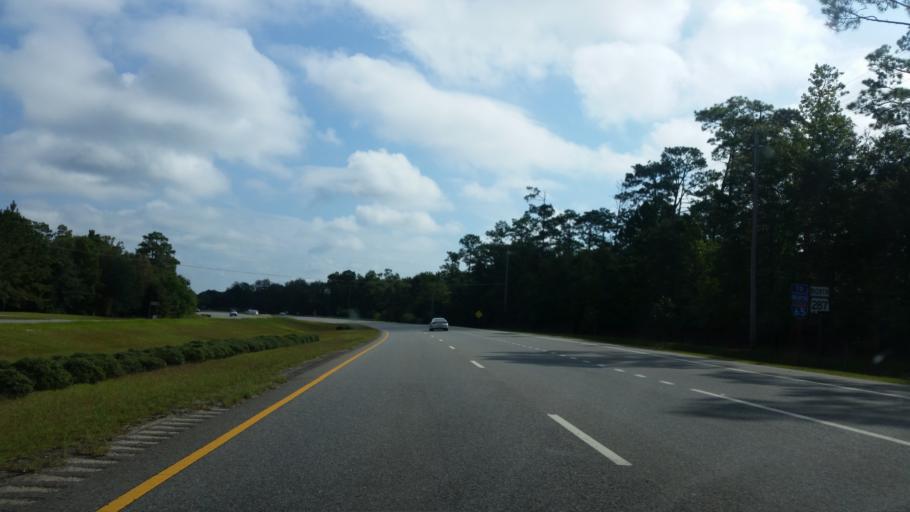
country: US
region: Alabama
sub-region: Baldwin County
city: Bay Minette
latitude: 30.9099
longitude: -87.7861
